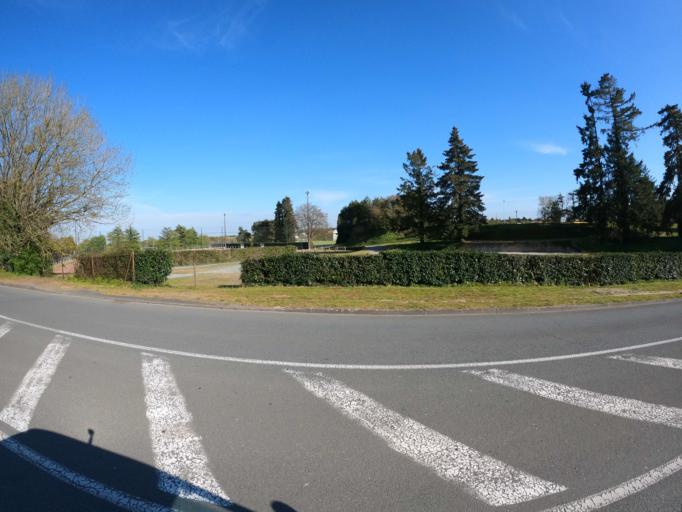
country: FR
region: Pays de la Loire
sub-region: Departement de la Vendee
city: La Verrie
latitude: 46.9656
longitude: -0.9934
